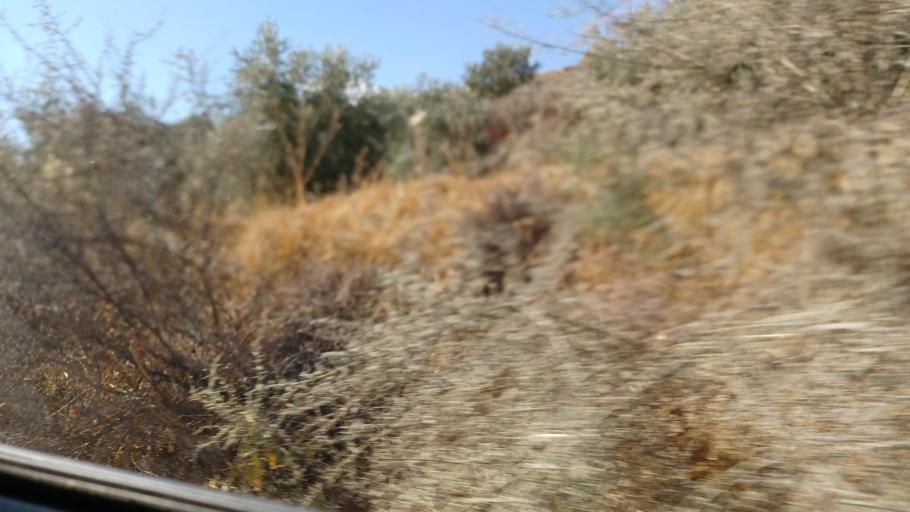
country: CY
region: Pafos
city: Polis
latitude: 34.9606
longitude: 32.4694
